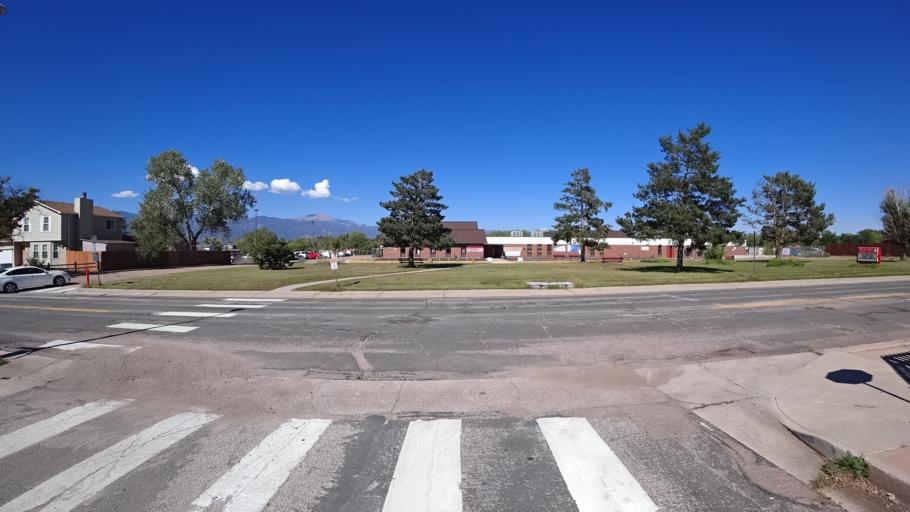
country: US
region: Colorado
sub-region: El Paso County
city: Stratmoor
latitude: 38.8159
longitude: -104.7392
